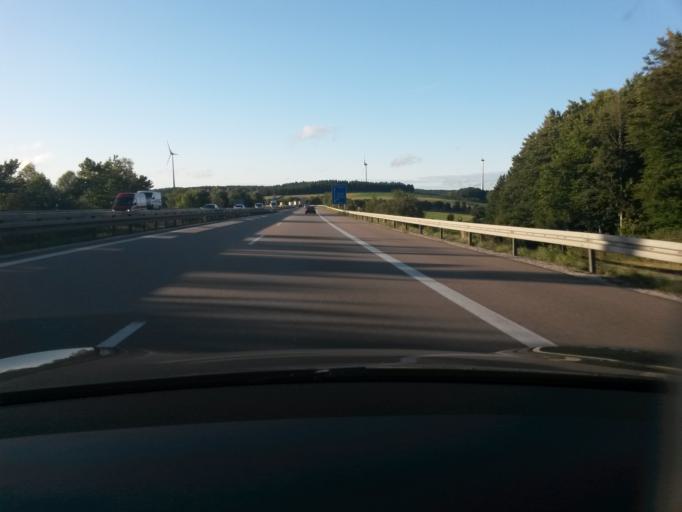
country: DE
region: Bavaria
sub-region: Upper Palatinate
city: Brunn
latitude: 49.1377
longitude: 11.8631
